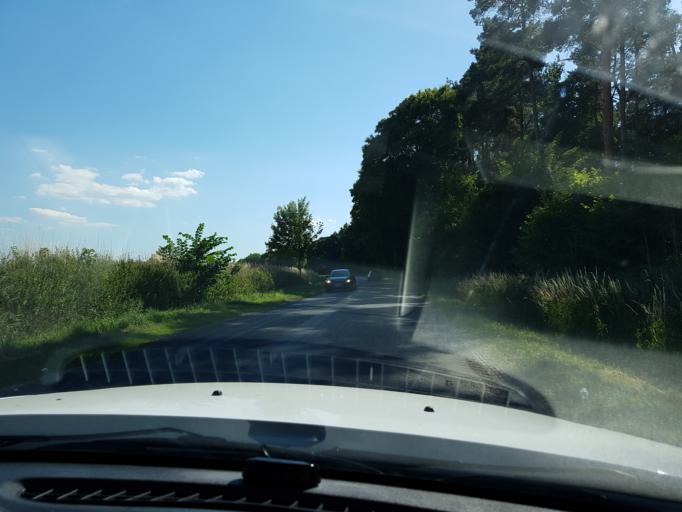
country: PL
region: West Pomeranian Voivodeship
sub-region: Powiat bialogardzki
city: Karlino
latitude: 53.9647
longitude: 15.9023
